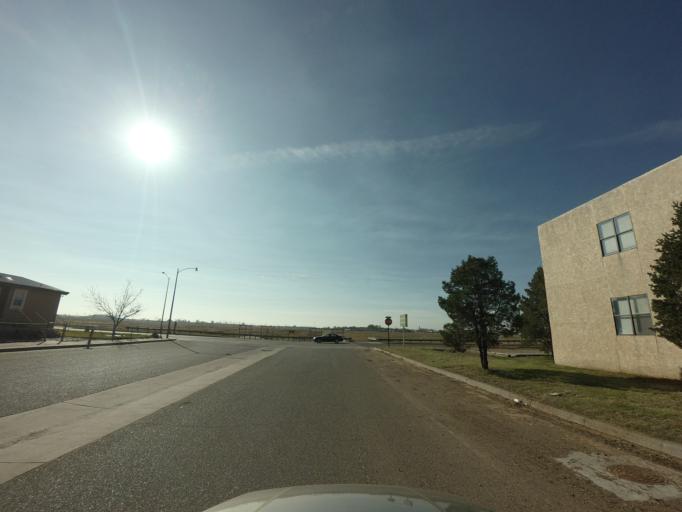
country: US
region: New Mexico
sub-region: Curry County
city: Clovis
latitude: 34.4052
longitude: -103.1752
